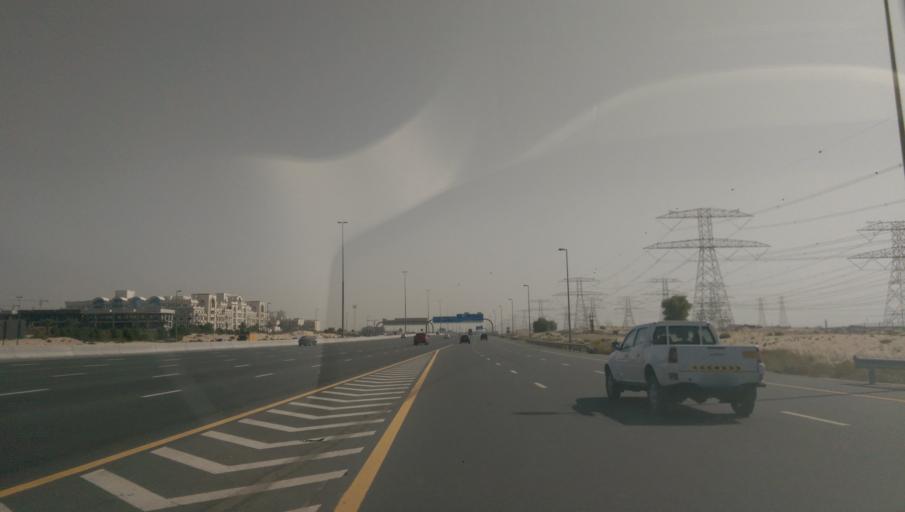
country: AE
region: Dubai
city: Dubai
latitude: 25.0720
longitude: 55.2060
